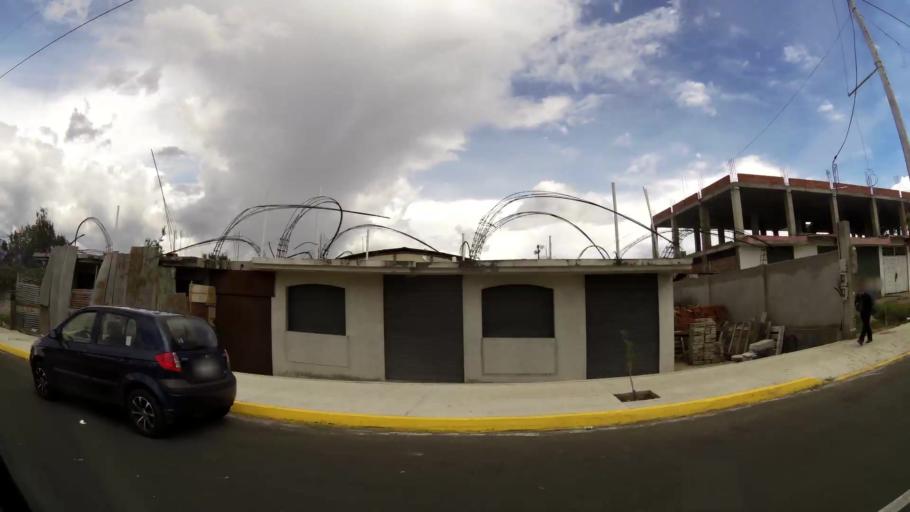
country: EC
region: Tungurahua
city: Ambato
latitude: -1.2662
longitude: -78.6090
